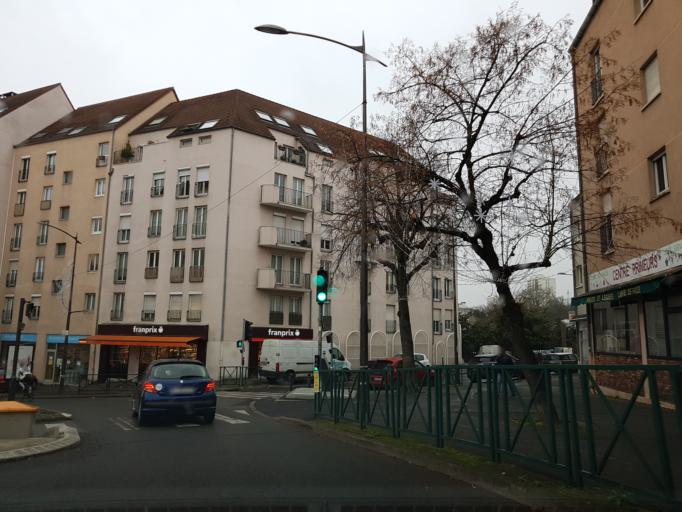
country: FR
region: Ile-de-France
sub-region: Departement du Val-de-Marne
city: Thiais
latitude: 48.7649
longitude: 2.3921
